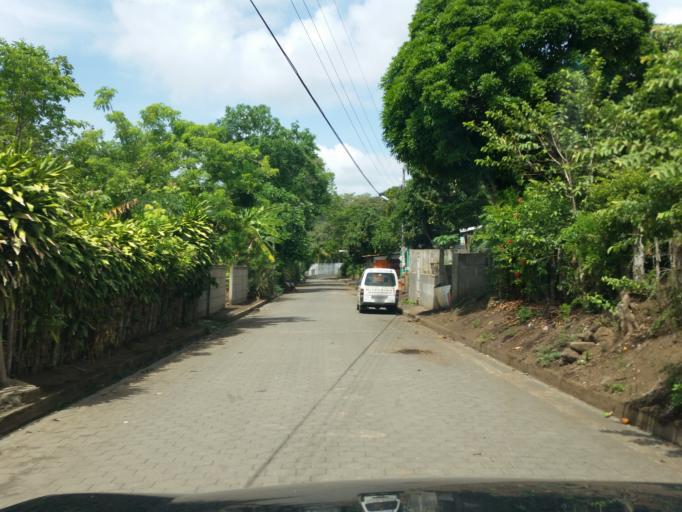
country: NI
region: Masaya
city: La Concepcion
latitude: 11.9505
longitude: -86.1850
